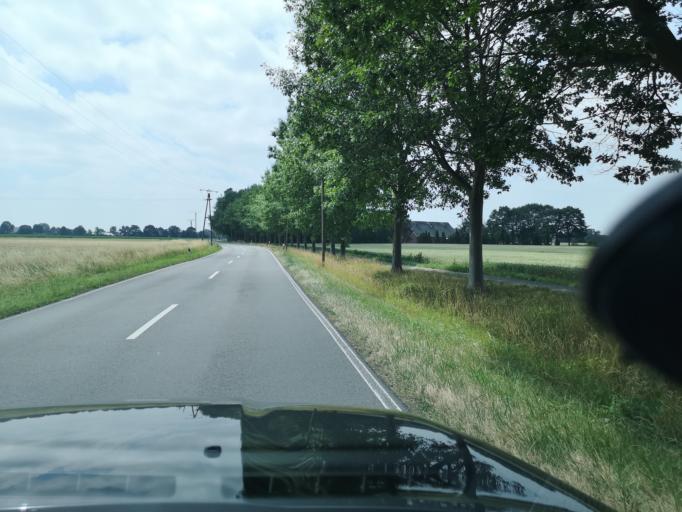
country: NL
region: Gelderland
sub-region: Gemeente Aalten
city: Aalten
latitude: 51.8721
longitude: 6.5619
